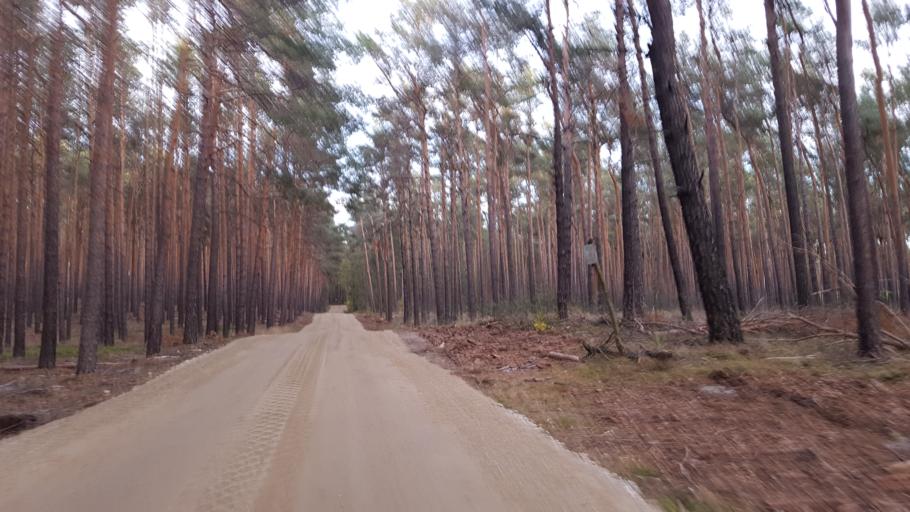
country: DE
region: Brandenburg
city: Trobitz
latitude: 51.5601
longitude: 13.4287
